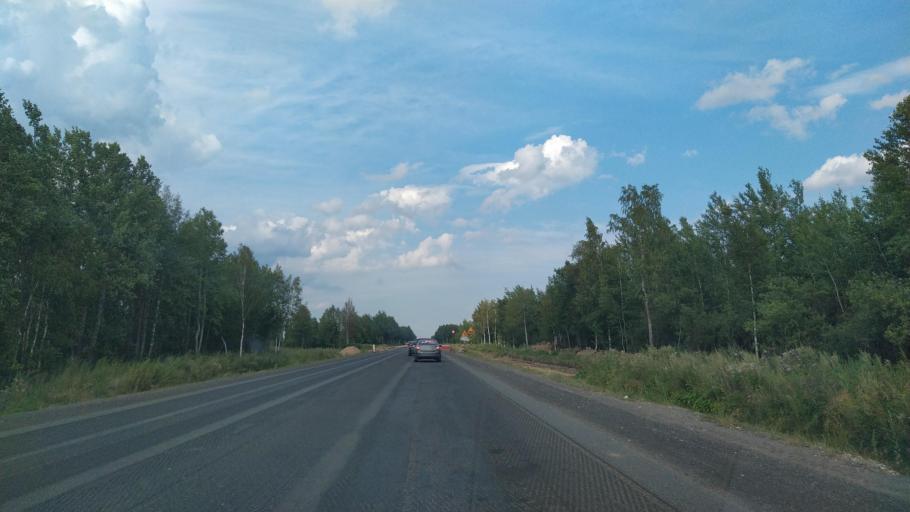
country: RU
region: Novgorod
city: Shimsk
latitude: 58.2913
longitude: 30.8602
